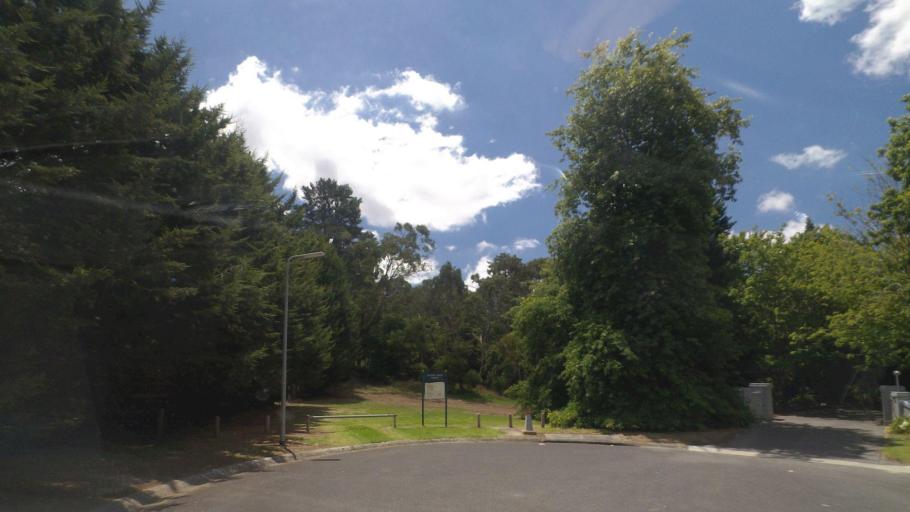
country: AU
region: Victoria
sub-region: Yarra Ranges
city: Chirnside Park
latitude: -37.7350
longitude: 145.2773
